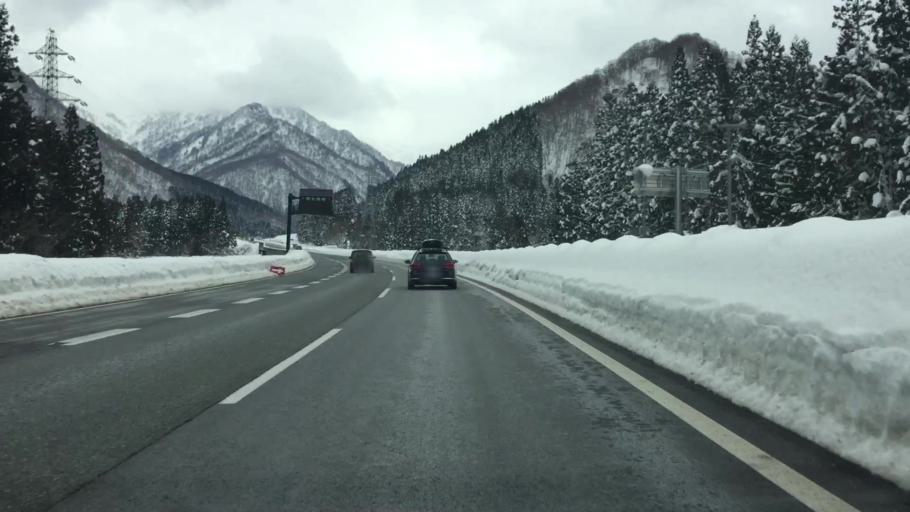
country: JP
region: Niigata
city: Shiozawa
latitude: 36.8819
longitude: 138.8535
